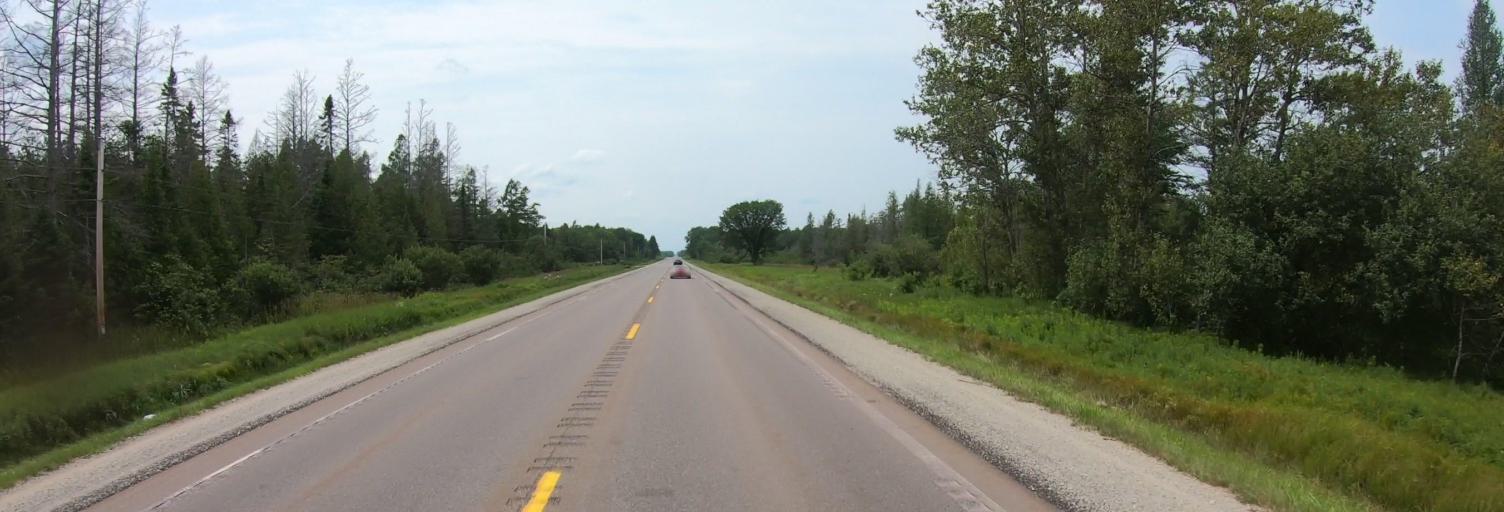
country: US
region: Michigan
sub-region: Marquette County
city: K. I. Sawyer Air Force Base
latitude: 46.3475
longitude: -87.0669
